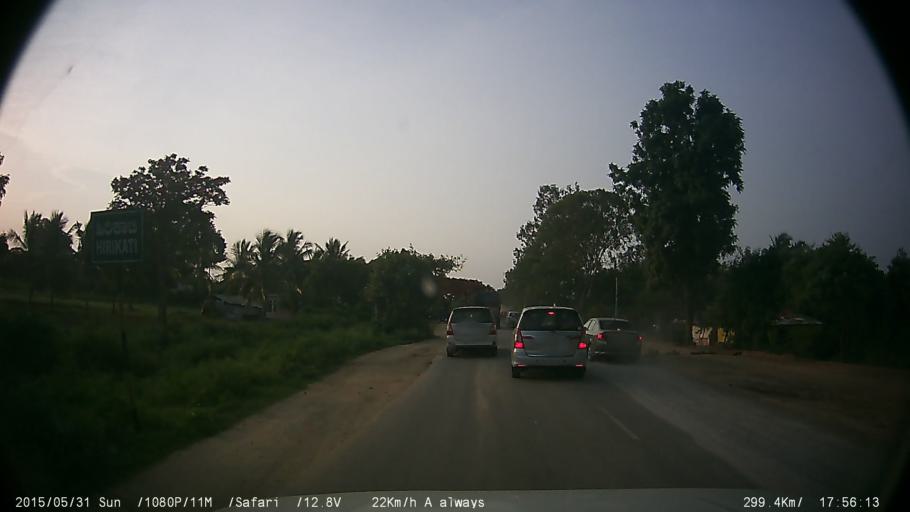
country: IN
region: Karnataka
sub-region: Mysore
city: Nanjangud
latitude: 11.9949
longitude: 76.6697
